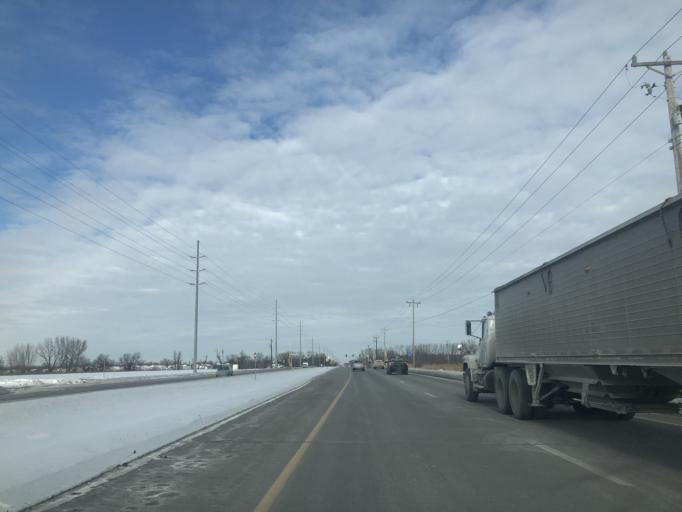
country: US
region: Minnesota
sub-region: Anoka County
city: Circle Pines
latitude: 45.1652
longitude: -93.1630
